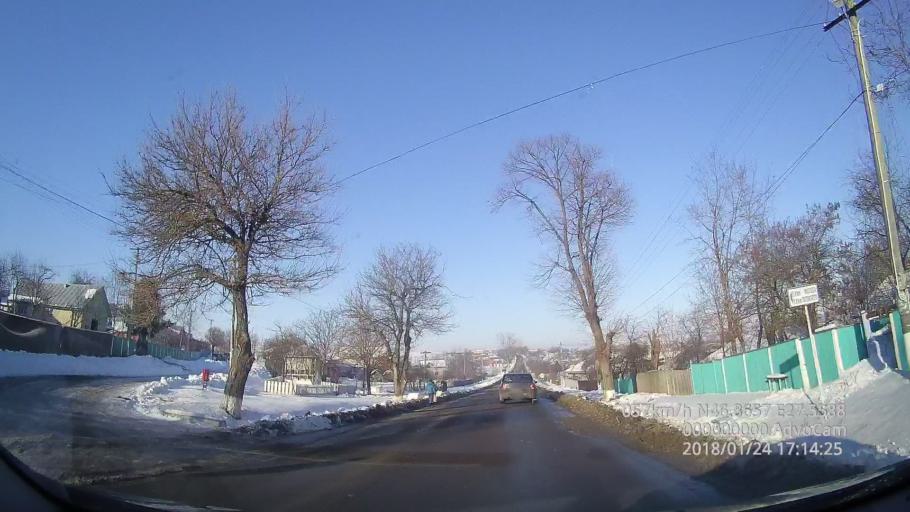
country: RO
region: Vaslui
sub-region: Comuna Rebricea
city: Rebricea
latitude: 46.8661
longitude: 27.5589
